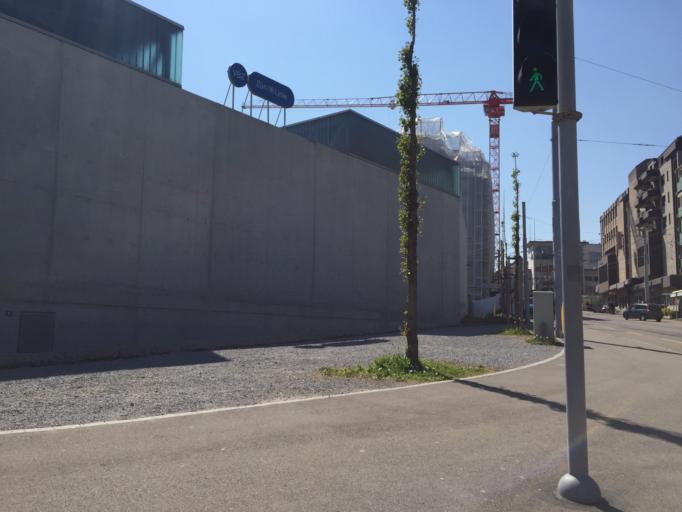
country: CH
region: Zurich
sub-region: Bezirk Zuerich
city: Zuerich (Kreis 11) / Oerlikon
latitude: 47.4103
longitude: 8.5483
